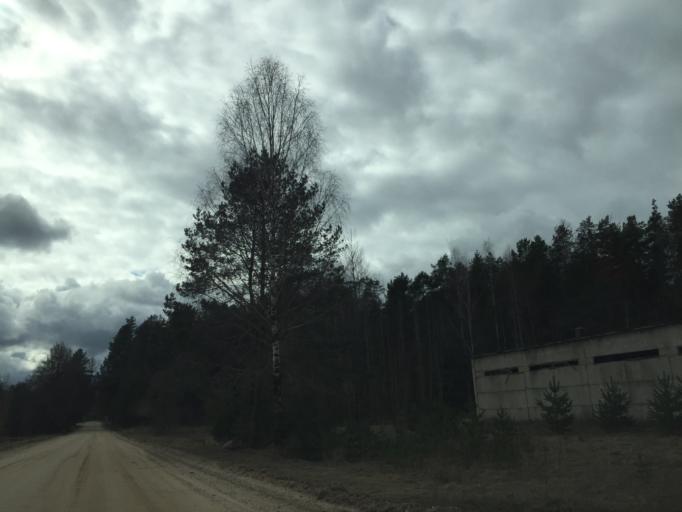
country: LV
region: Akniste
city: Akniste
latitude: 56.1037
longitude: 25.8236
